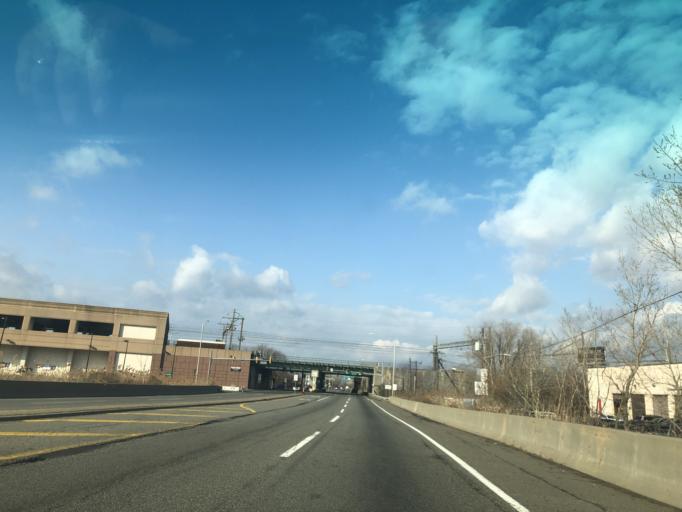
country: US
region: New Jersey
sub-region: Hudson County
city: Secaucus
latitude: 40.7612
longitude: -74.0722
